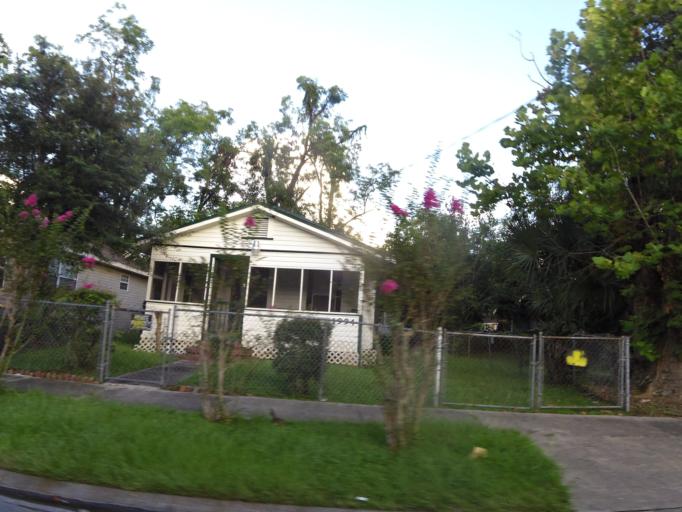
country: US
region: Florida
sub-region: Duval County
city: Jacksonville
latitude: 30.3360
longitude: -81.6936
